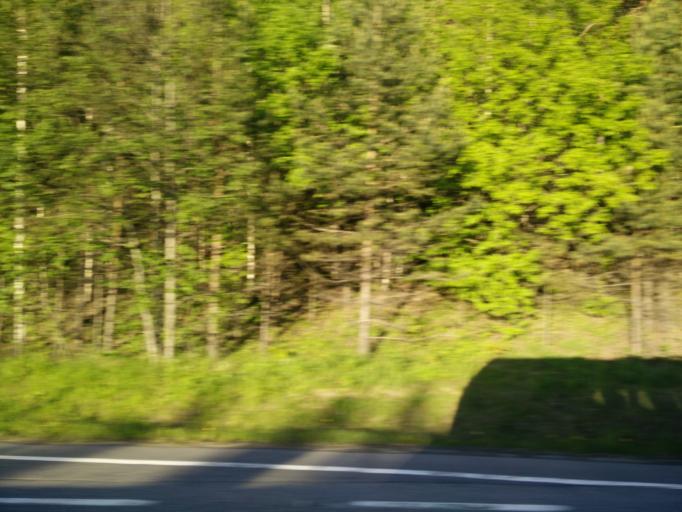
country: NO
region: Buskerud
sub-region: Hole
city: Vik
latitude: 60.0247
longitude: 10.2683
